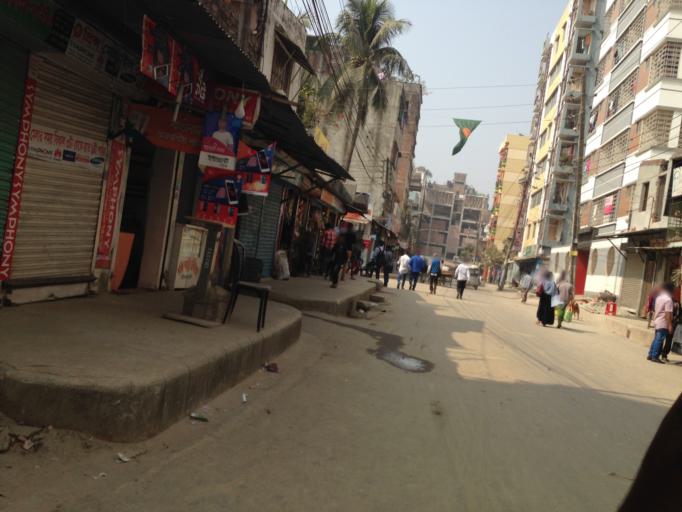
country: BD
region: Dhaka
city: Azimpur
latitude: 23.8081
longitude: 90.3805
